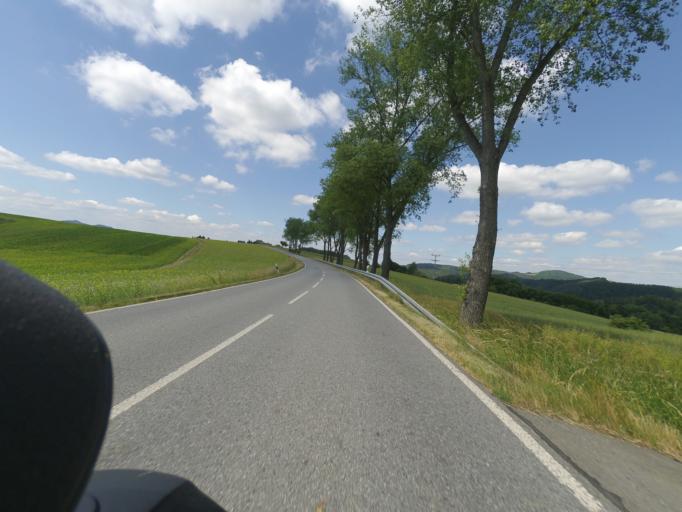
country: DE
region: Saxony
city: Bad Schandau
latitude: 50.9373
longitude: 14.1897
